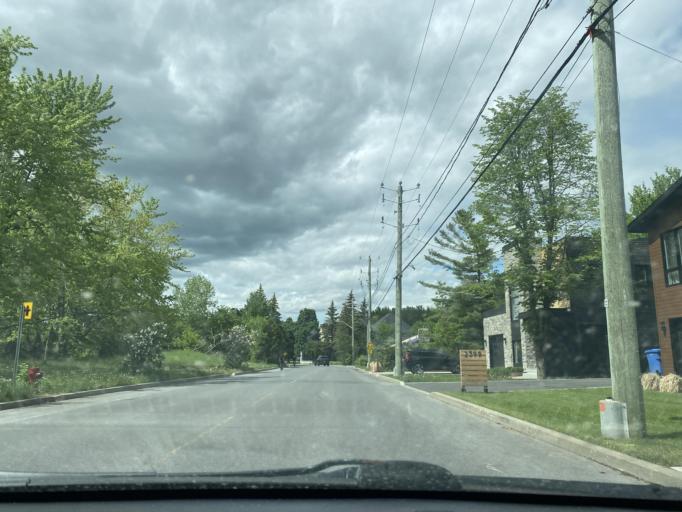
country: CA
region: Quebec
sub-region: Monteregie
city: Carignan
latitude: 45.4655
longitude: -73.2934
